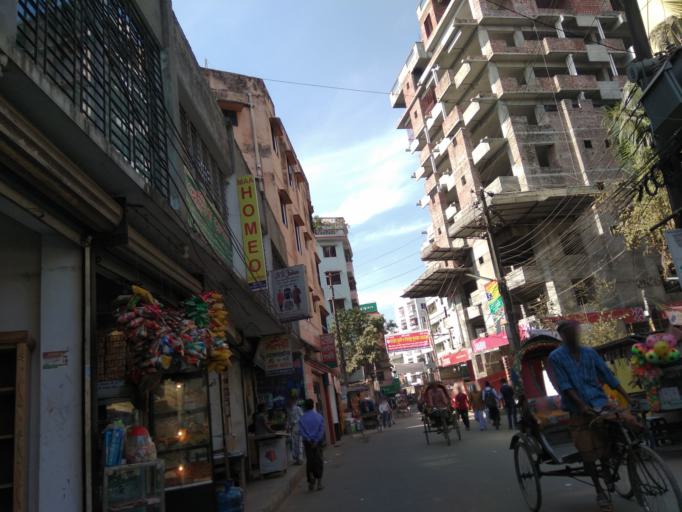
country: BD
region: Dhaka
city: Azimpur
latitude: 23.7732
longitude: 90.3595
